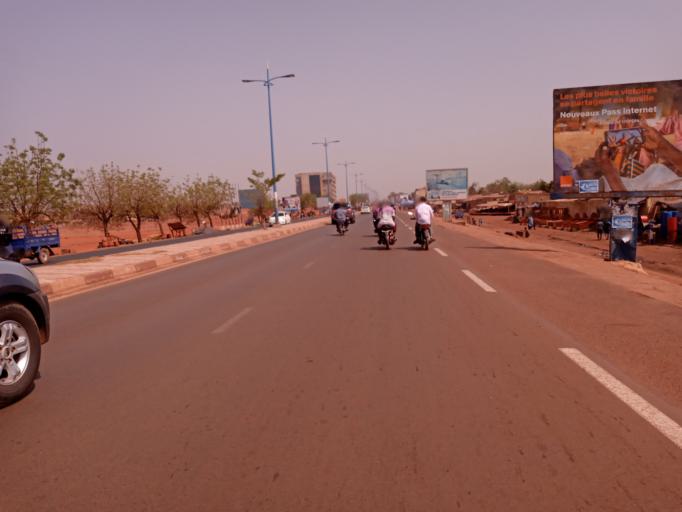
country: ML
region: Bamako
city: Bamako
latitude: 12.5955
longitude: -7.9923
